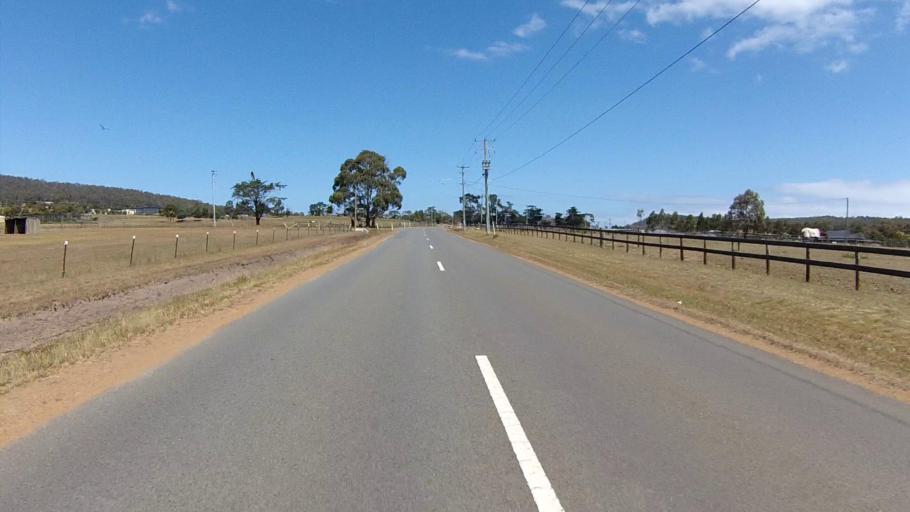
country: AU
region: Tasmania
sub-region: Clarence
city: Sandford
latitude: -42.9508
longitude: 147.4810
